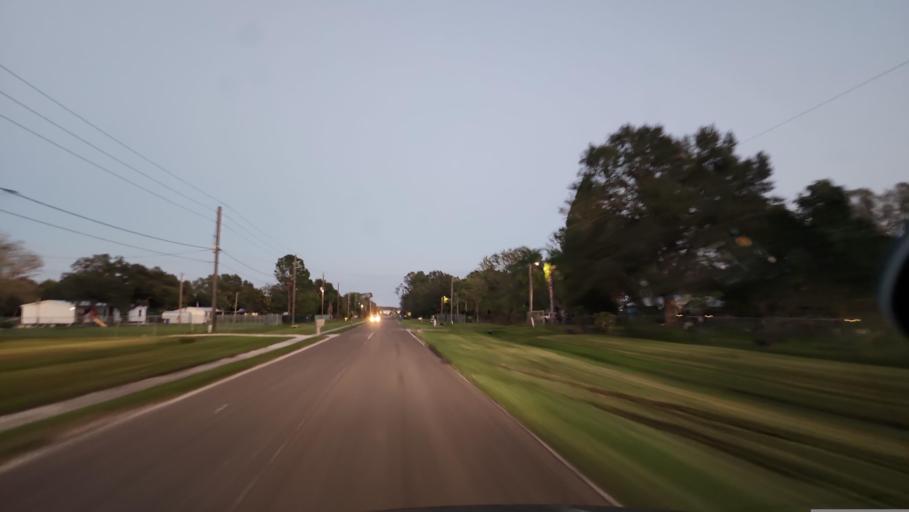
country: US
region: Florida
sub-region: Hillsborough County
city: Balm
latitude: 27.8013
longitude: -82.2794
